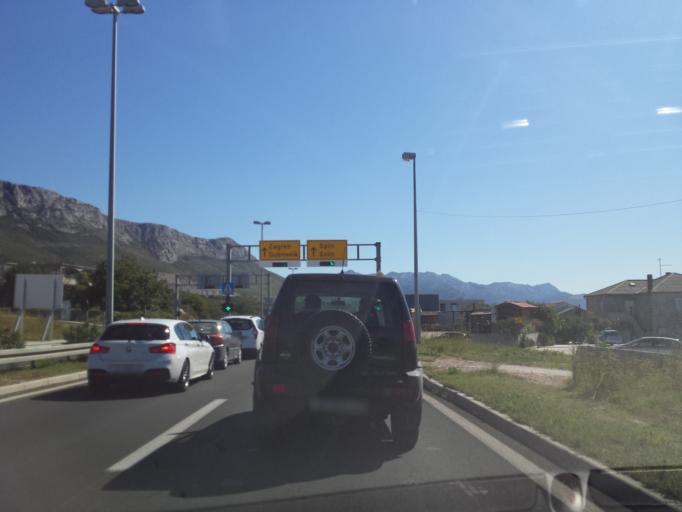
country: HR
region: Splitsko-Dalmatinska
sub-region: Grad Split
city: Split
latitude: 43.5509
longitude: 16.4211
